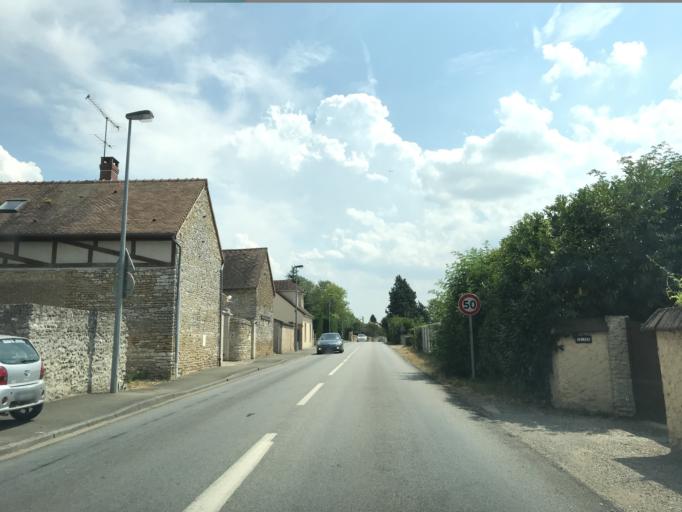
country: FR
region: Haute-Normandie
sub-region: Departement de l'Eure
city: Breuilpont
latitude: 48.9773
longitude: 1.4221
